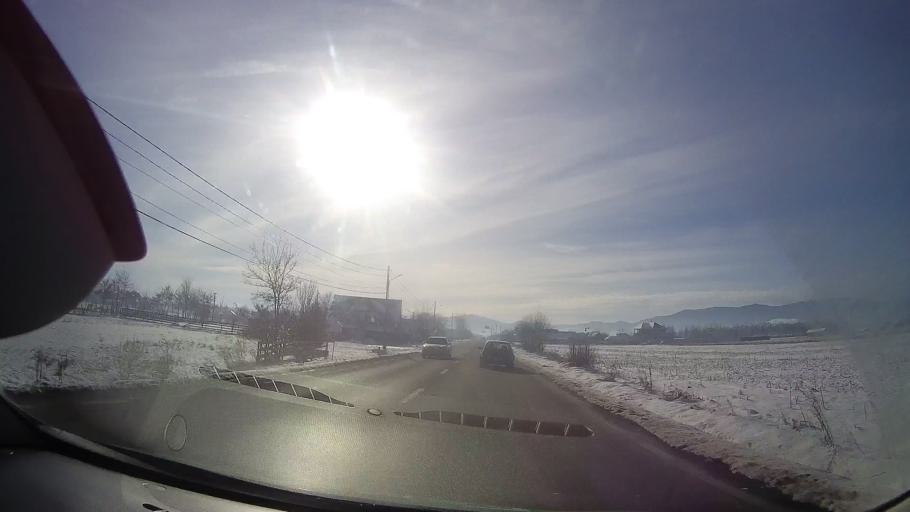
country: RO
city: Vanatori-Neamt
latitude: 47.1767
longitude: 26.3275
